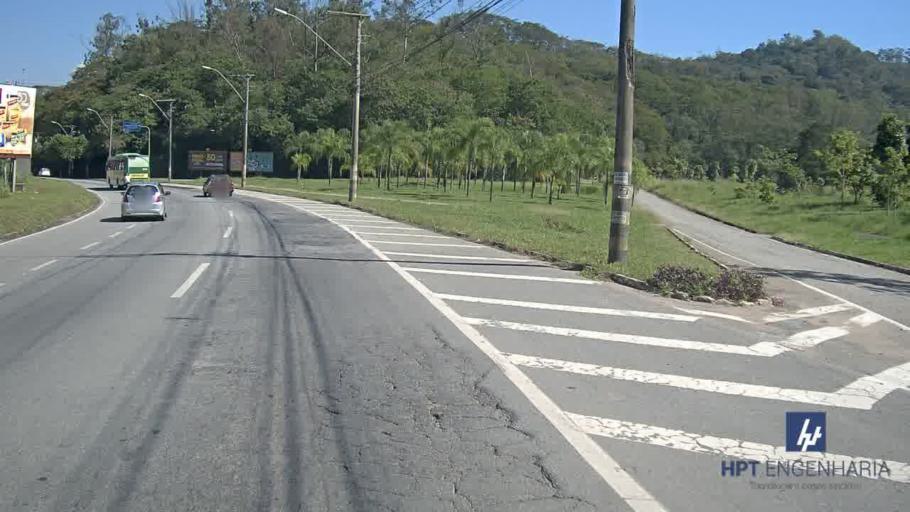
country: BR
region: Minas Gerais
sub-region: Ipatinga
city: Ipatinga
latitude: -19.4912
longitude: -42.5635
